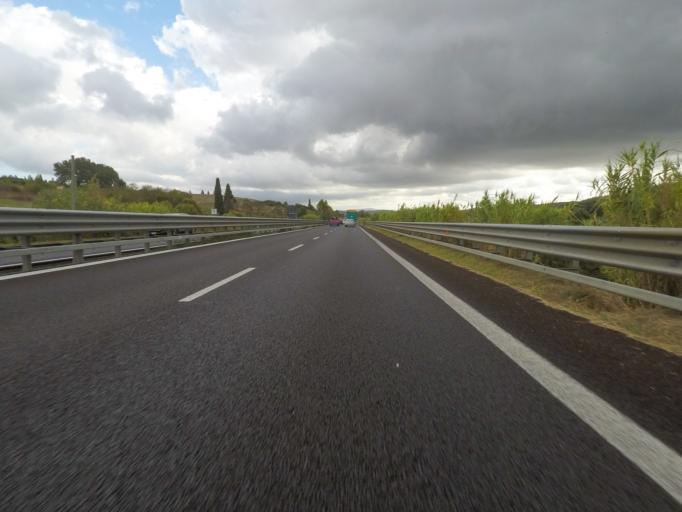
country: IT
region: Tuscany
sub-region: Provincia di Siena
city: Arbia
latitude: 43.3061
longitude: 11.4364
